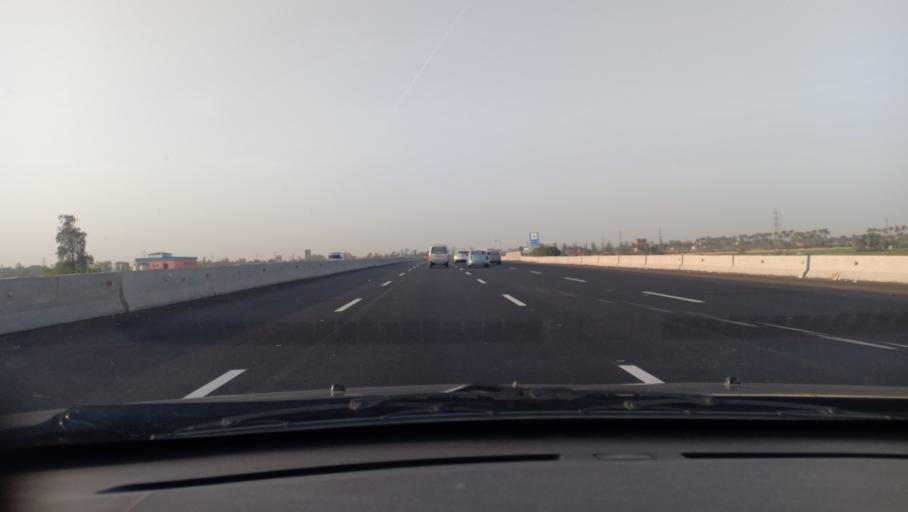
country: EG
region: Muhafazat al Qalyubiyah
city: Toukh
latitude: 30.2982
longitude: 31.2188
